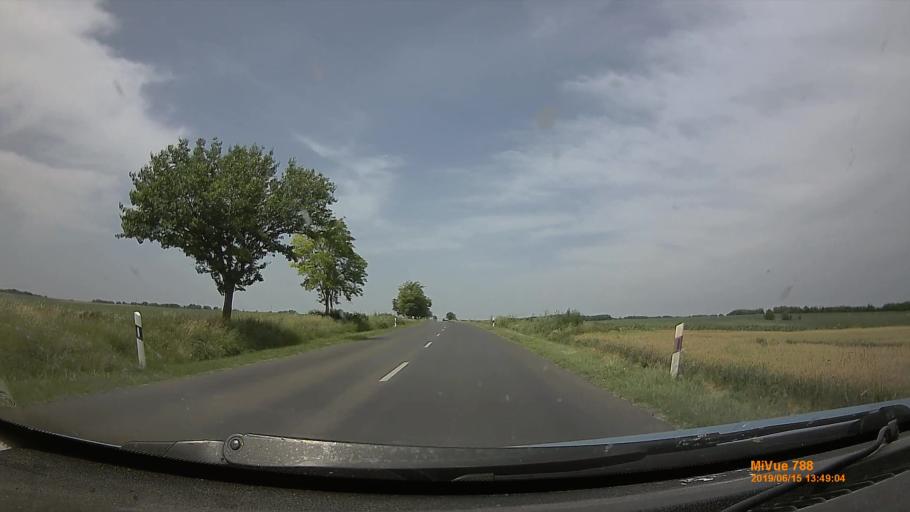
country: HU
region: Tolna
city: Iregszemcse
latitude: 46.7242
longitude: 18.1708
